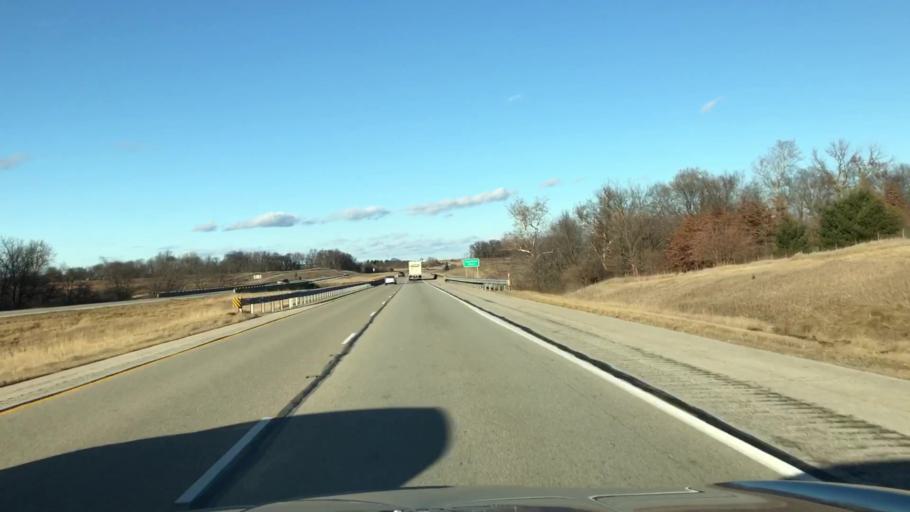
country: US
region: Illinois
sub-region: McLean County
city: Lexington
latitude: 40.6285
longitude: -88.8164
